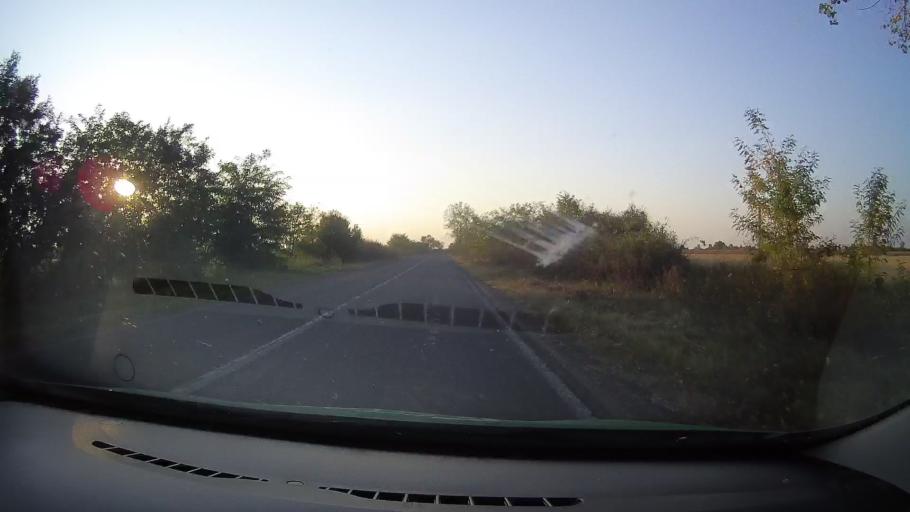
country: RO
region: Arad
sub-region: Comuna Bocsig
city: Bocsig
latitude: 46.4254
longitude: 21.9134
